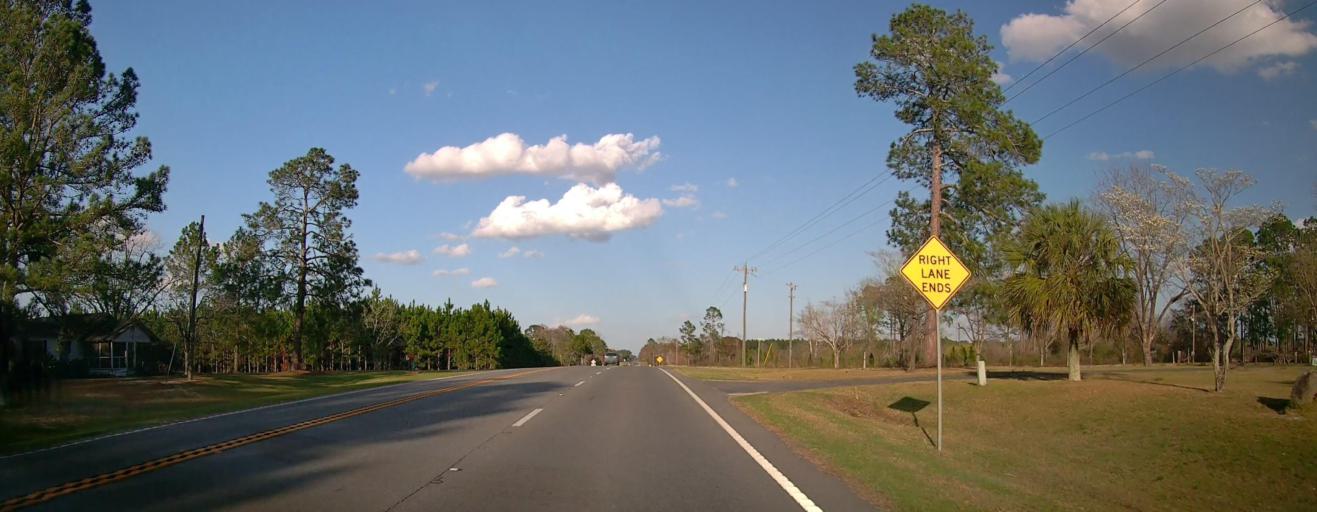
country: US
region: Georgia
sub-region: Tattnall County
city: Reidsville
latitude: 32.1119
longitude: -82.0825
